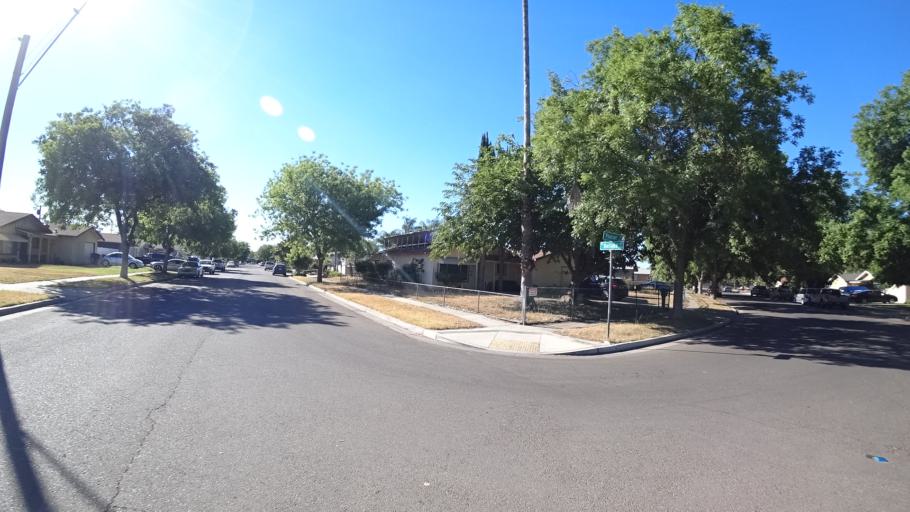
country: US
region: California
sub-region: Fresno County
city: Fresno
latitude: 36.7967
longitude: -119.8393
